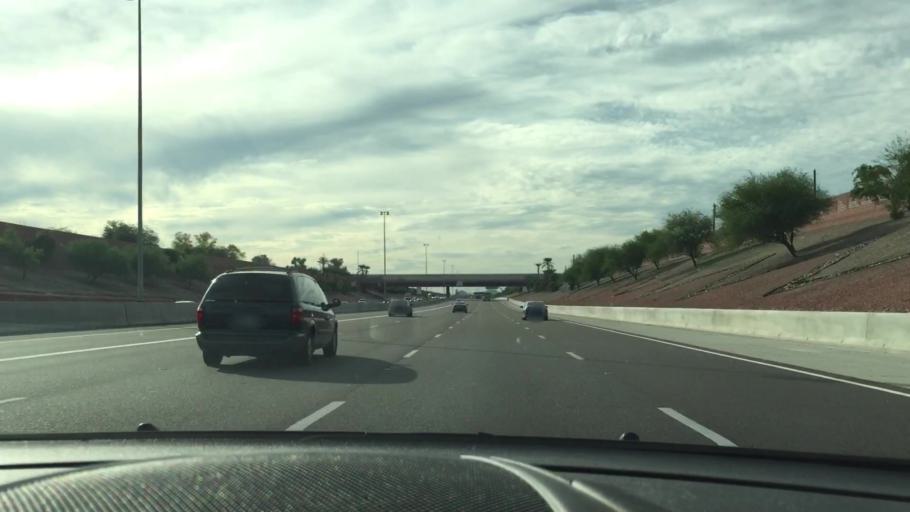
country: US
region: Arizona
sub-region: Maricopa County
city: Mesa
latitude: 33.4646
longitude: -111.8003
